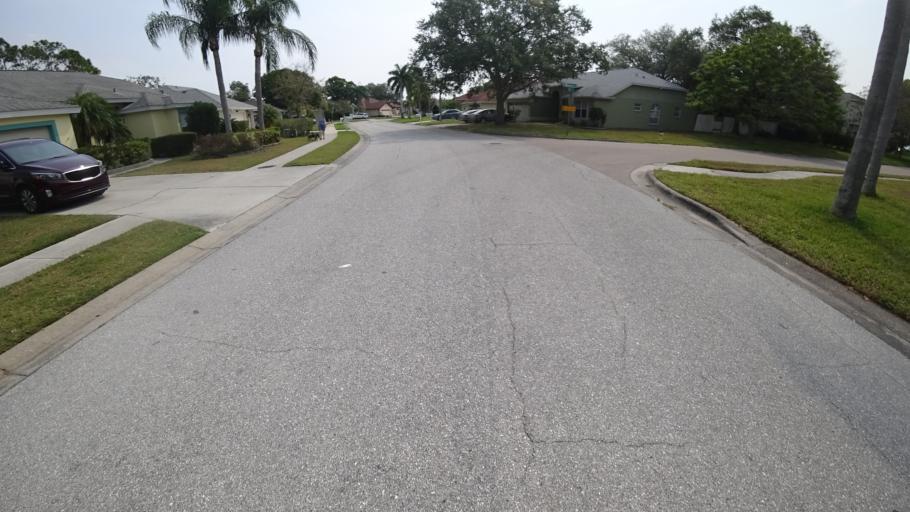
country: US
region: Florida
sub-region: Manatee County
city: Samoset
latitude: 27.4604
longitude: -82.5088
